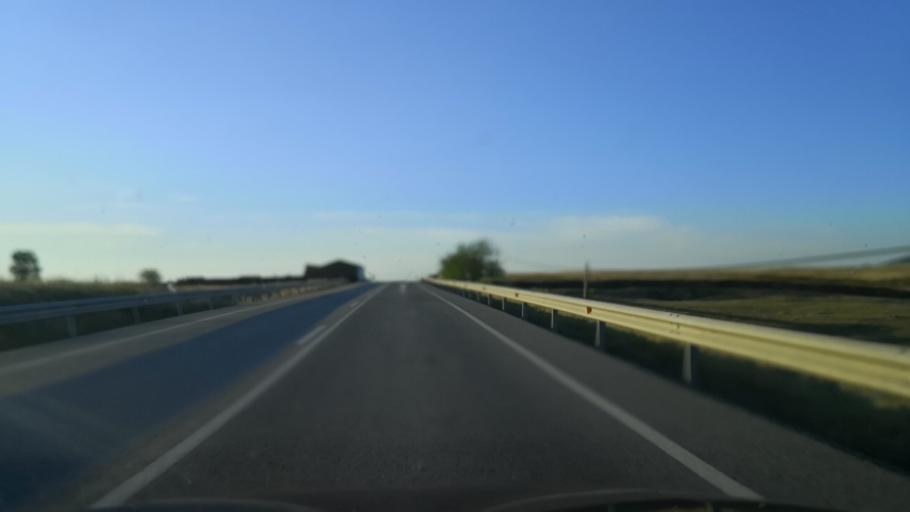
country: ES
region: Extremadura
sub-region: Provincia de Caceres
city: Valencia de Alcantara
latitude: 39.4404
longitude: -7.2243
